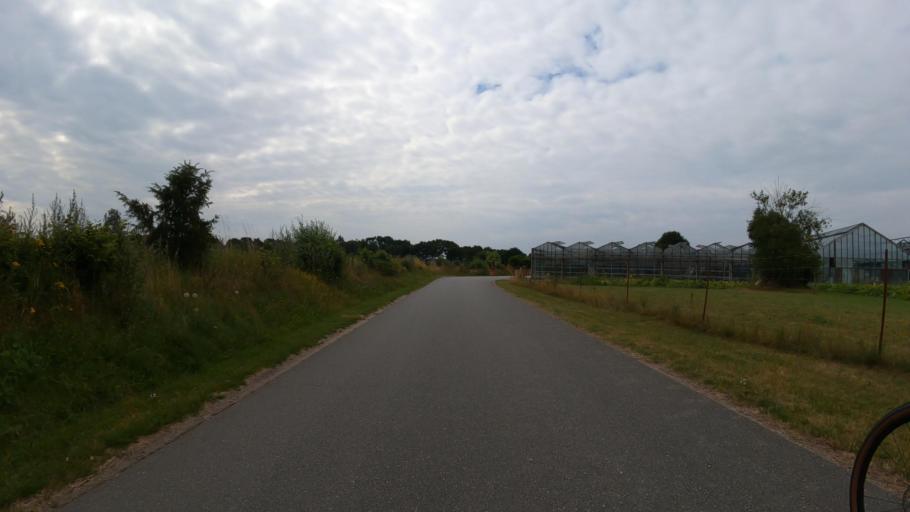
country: DE
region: Schleswig-Holstein
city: Gross Kummerfeld
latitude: 54.0341
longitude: 10.0590
